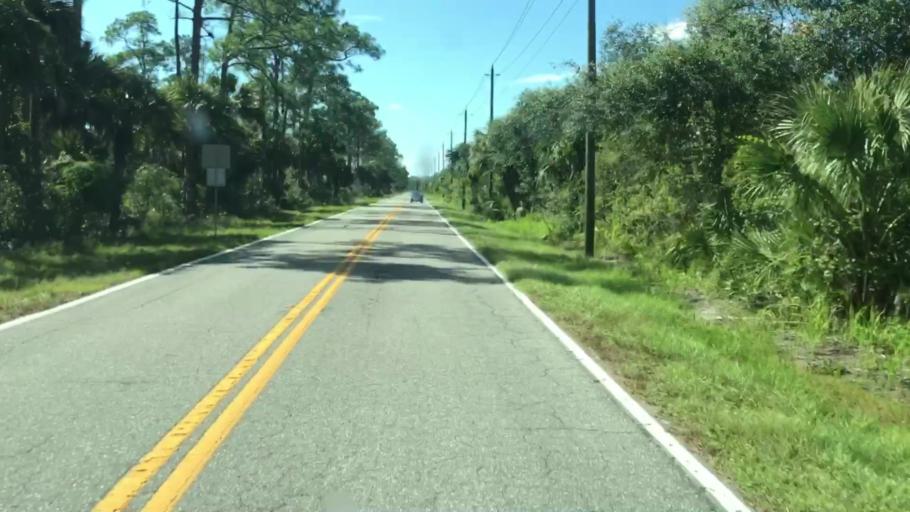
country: US
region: Florida
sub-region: Lee County
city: Alva
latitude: 26.7254
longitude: -81.6567
